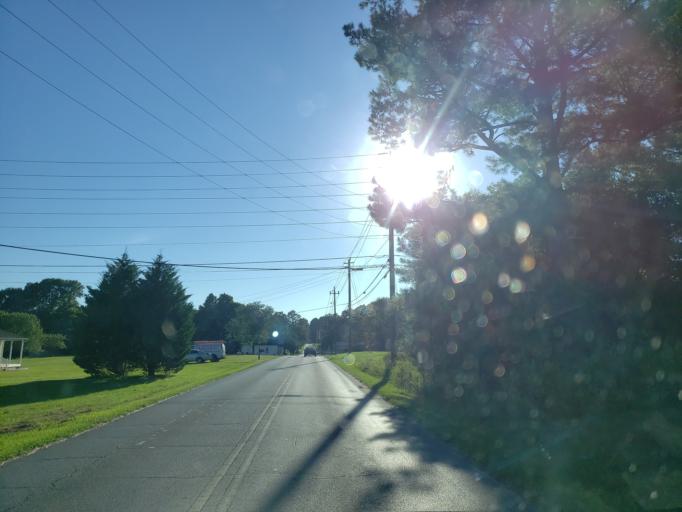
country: US
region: Georgia
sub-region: Polk County
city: Aragon
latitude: 34.0423
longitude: -85.0607
